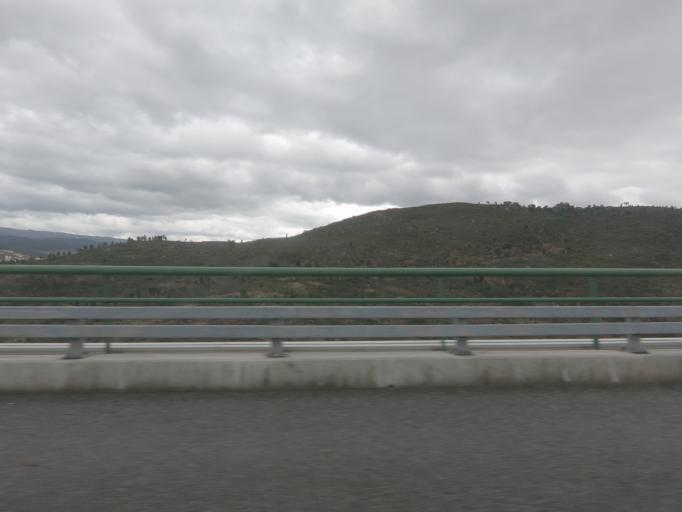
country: PT
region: Vila Real
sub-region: Boticas
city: Boticas
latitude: 41.6394
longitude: -7.5919
